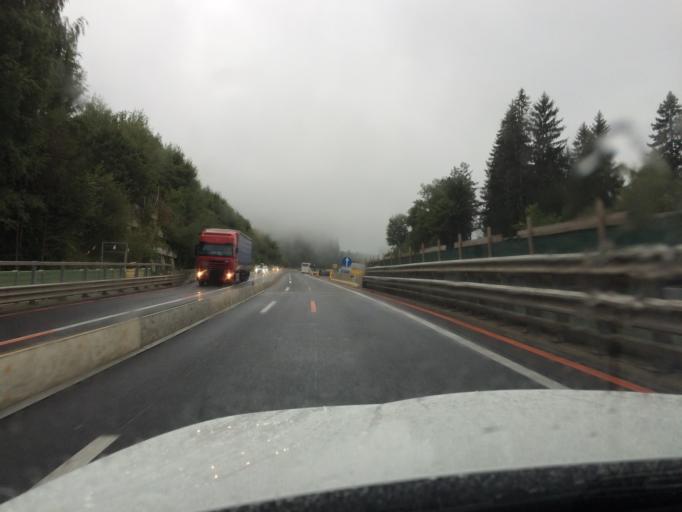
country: AT
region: Styria
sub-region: Politischer Bezirk Voitsberg
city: Voitsberg
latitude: 46.9795
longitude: 15.1171
